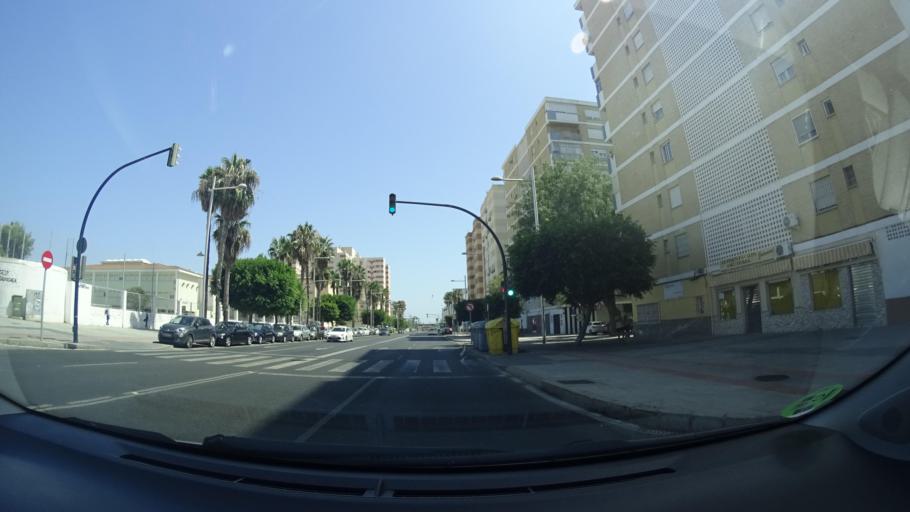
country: ES
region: Andalusia
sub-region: Provincia de Cadiz
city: Cadiz
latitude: 36.5066
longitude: -6.2738
